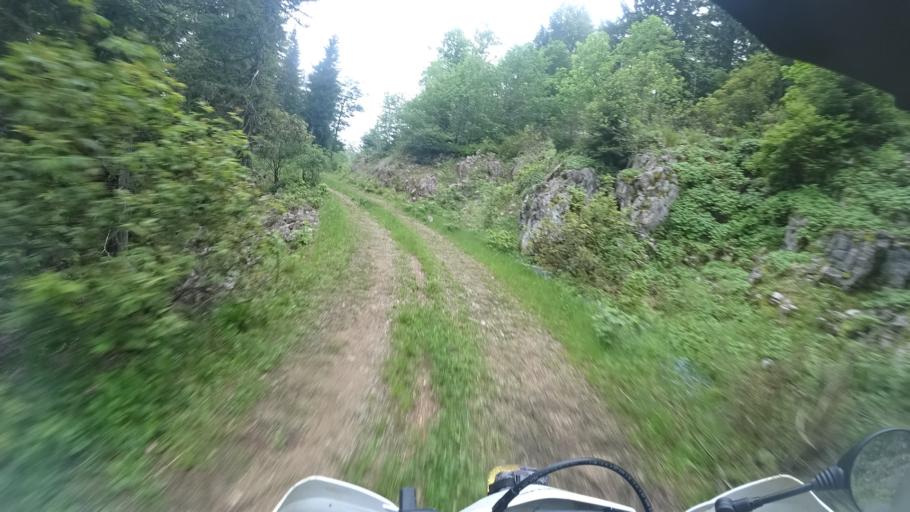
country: BA
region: Federation of Bosnia and Herzegovina
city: Bihac
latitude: 44.6264
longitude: 15.8309
